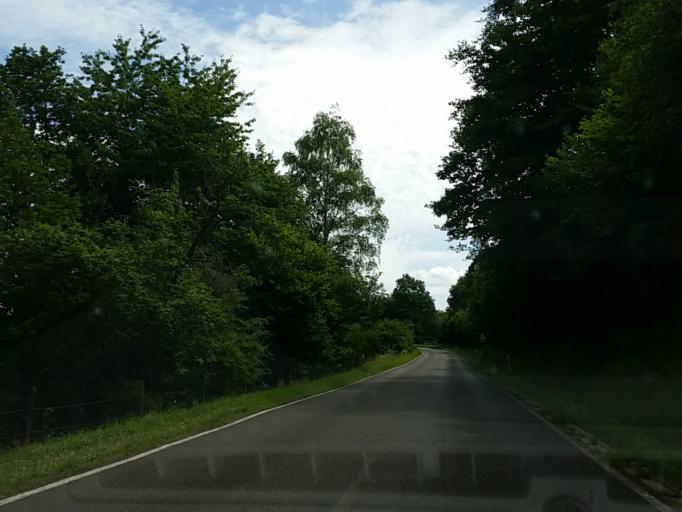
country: DE
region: Rheinland-Pfalz
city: Irsch
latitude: 49.5746
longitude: 6.6077
